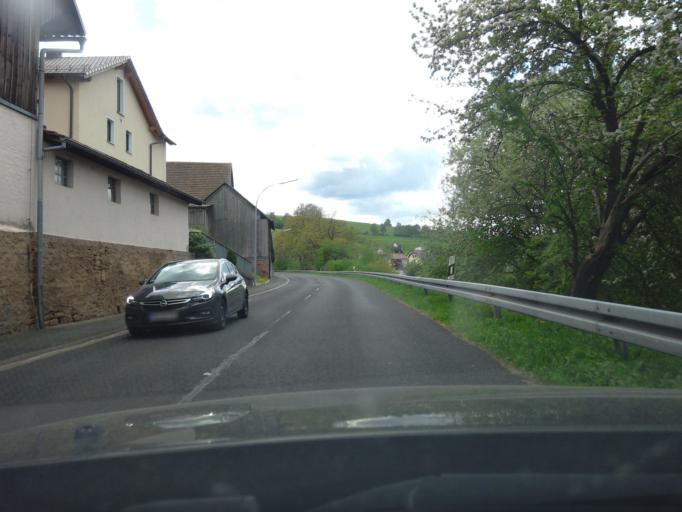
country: DE
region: Bavaria
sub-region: Regierungsbezirk Unterfranken
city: Aura im Sinngrund
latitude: 50.1673
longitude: 9.4738
